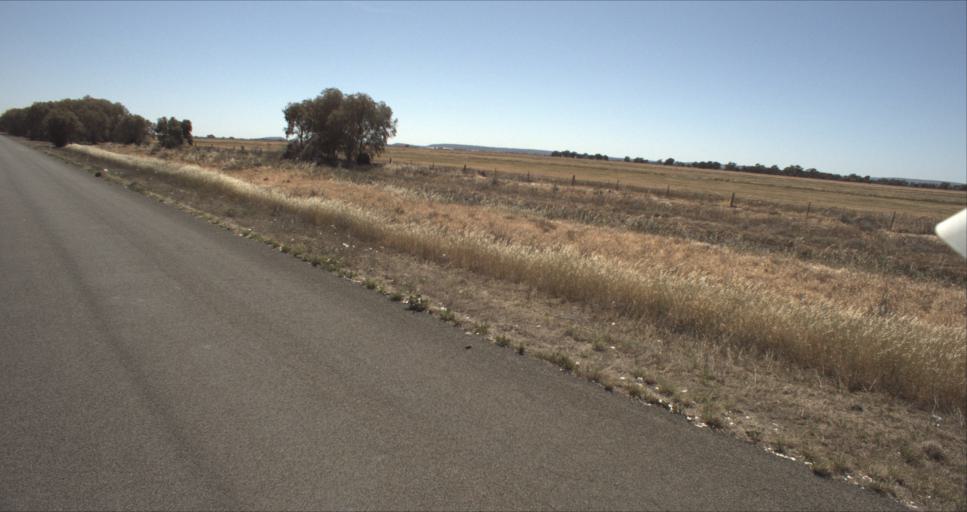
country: AU
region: New South Wales
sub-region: Leeton
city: Leeton
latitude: -34.4884
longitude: 146.2892
